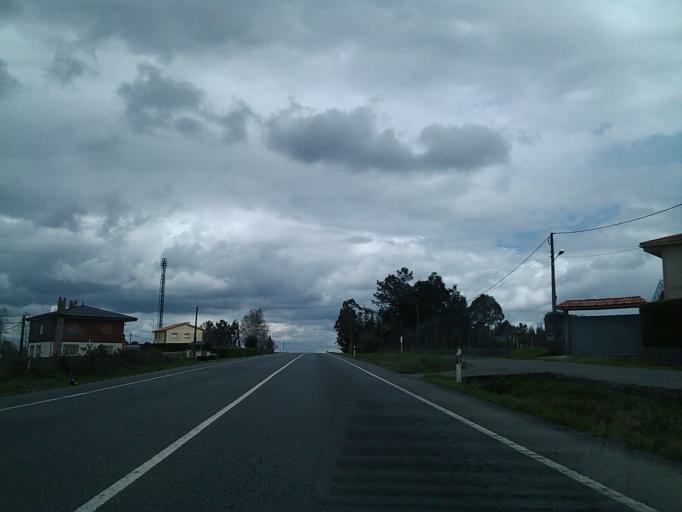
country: ES
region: Galicia
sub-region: Provincia da Coruna
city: Curtis
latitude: 43.1396
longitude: -8.0278
